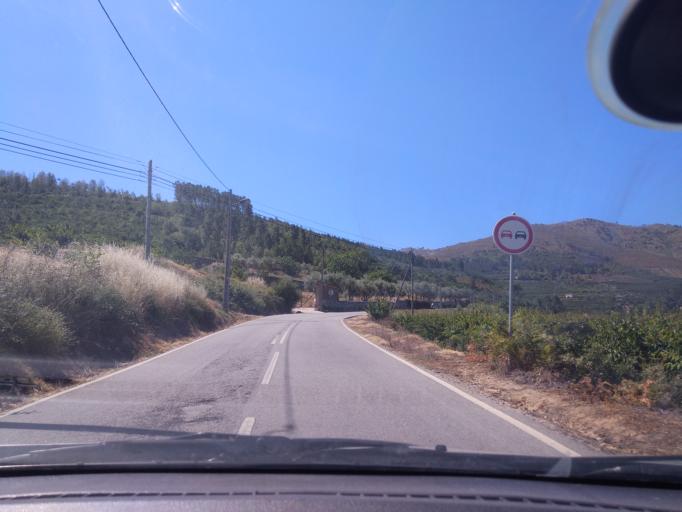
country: PT
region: Castelo Branco
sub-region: Concelho do Fundao
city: Fundao
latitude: 40.1275
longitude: -7.4870
